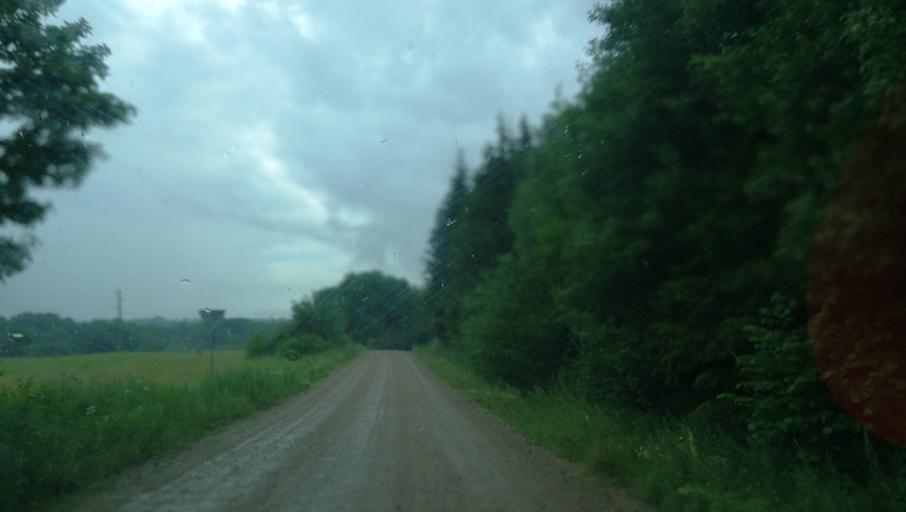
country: LV
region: Vecpiebalga
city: Vecpiebalga
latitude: 57.1110
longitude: 25.6920
